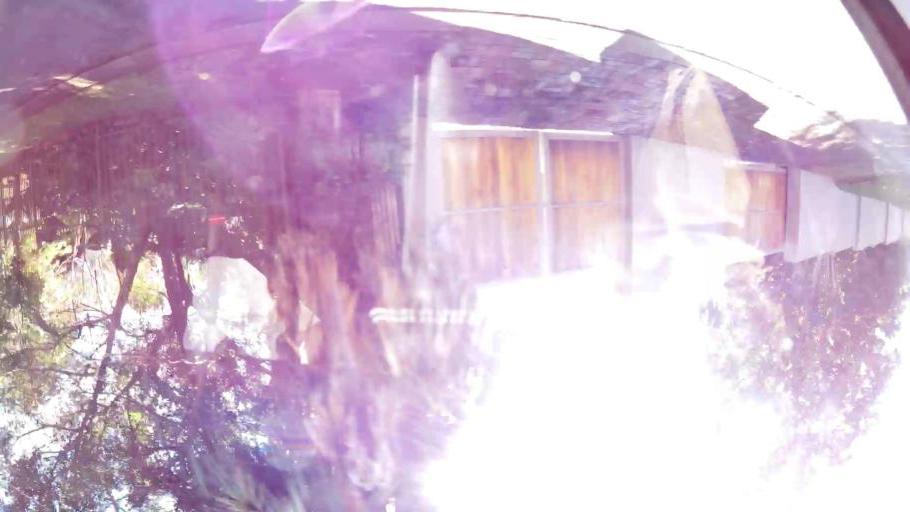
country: ZA
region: Limpopo
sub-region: Mopani District Municipality
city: Tzaneen
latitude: -23.8122
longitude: 30.1510
